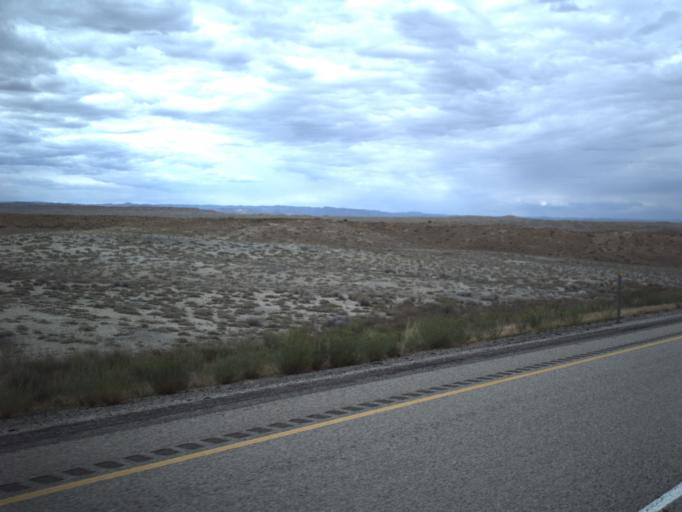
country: US
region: Utah
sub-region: Grand County
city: Moab
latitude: 38.9709
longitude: -109.3594
